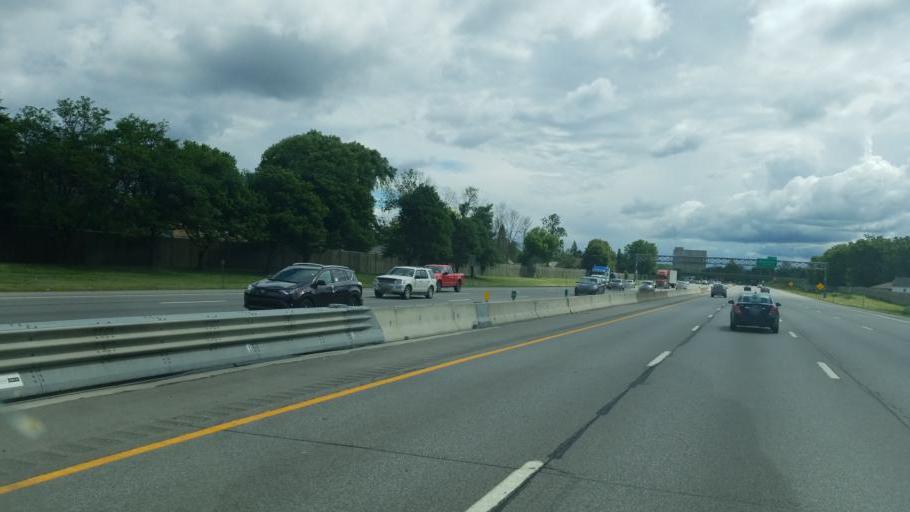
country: US
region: New York
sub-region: Erie County
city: Sloan
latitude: 42.8775
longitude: -78.7803
